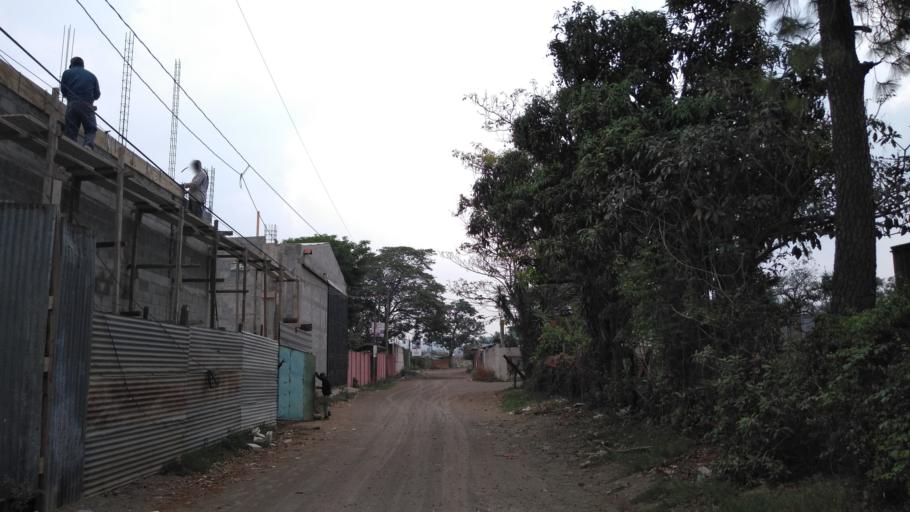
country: GT
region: Guatemala
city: Petapa
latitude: 14.5115
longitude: -90.5568
